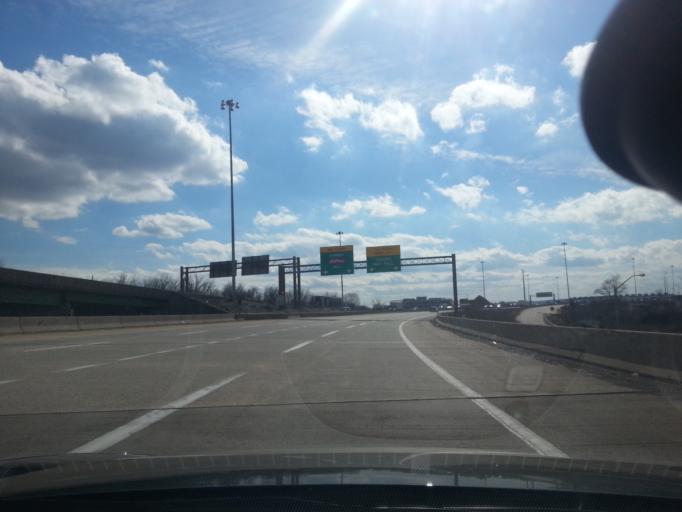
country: US
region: Pennsylvania
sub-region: Montgomery County
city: Plymouth Meeting
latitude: 40.1108
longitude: -75.2797
